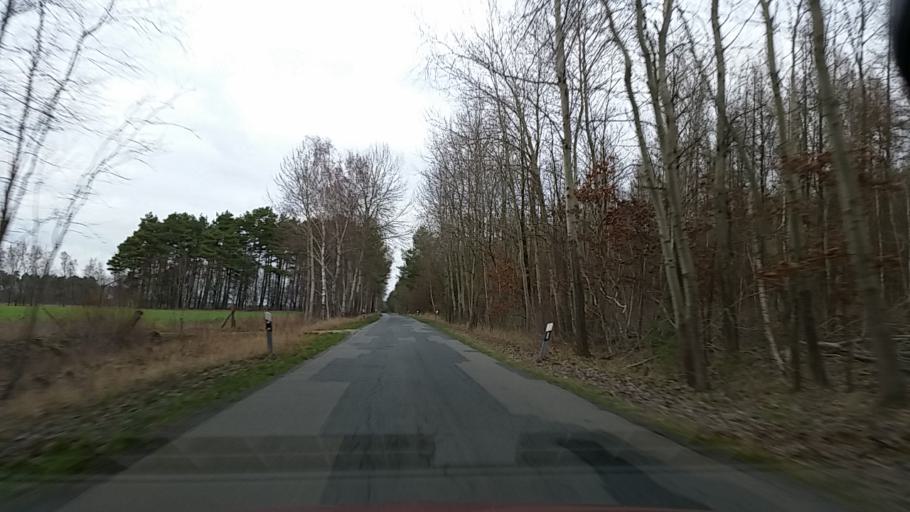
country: DE
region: Lower Saxony
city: Luder
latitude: 52.7870
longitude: 10.6693
